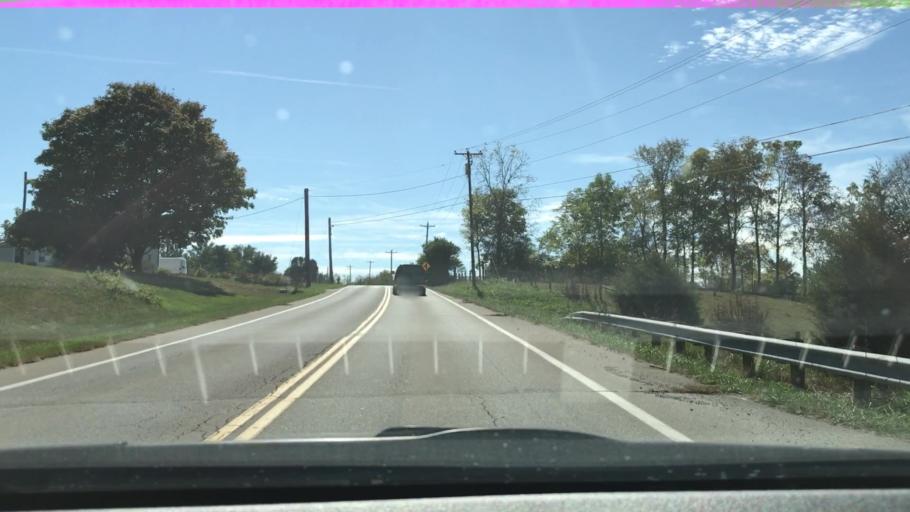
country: US
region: Ohio
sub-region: Butler County
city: Hamilton
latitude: 39.4595
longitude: -84.6273
